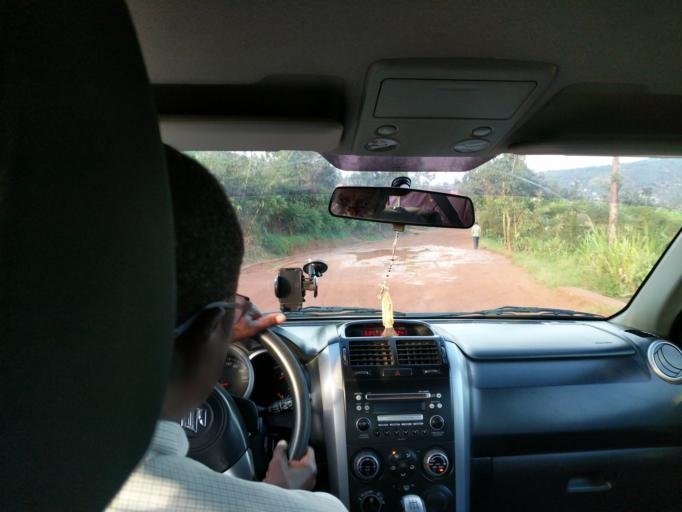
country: RW
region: Kigali
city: Kigali
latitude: -2.0128
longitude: 30.0393
